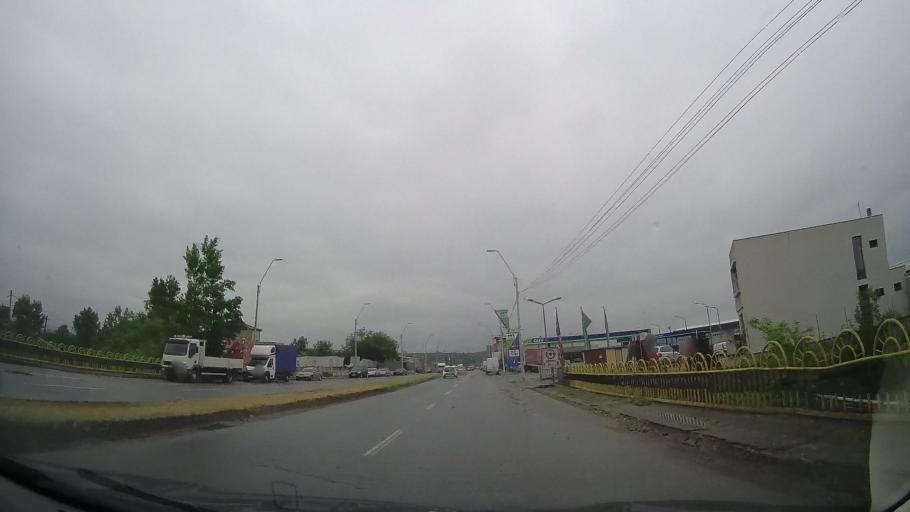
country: RO
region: Mehedinti
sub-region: Comuna Simian
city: Cerneti
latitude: 44.6310
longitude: 22.6852
